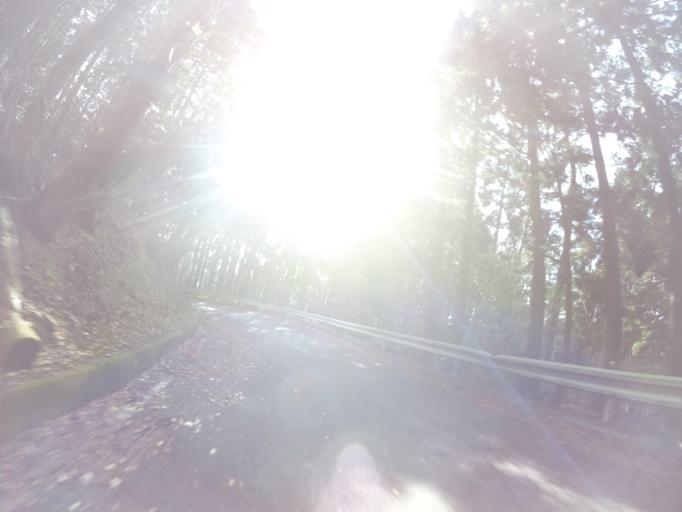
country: JP
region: Shizuoka
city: Heda
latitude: 34.8360
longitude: 138.8475
